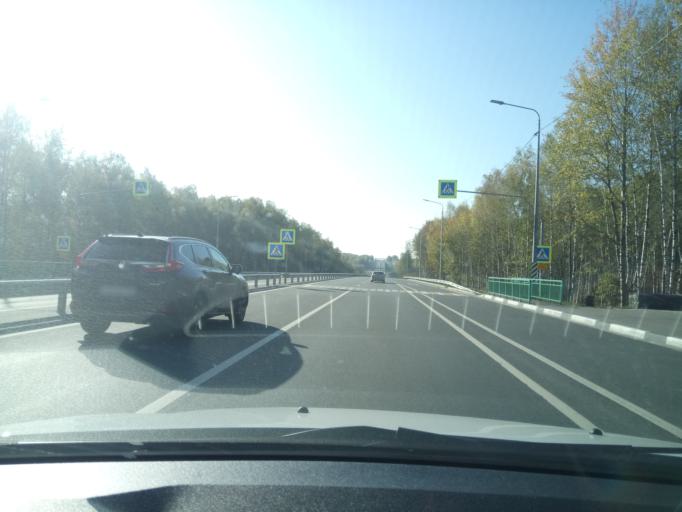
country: RU
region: Nizjnij Novgorod
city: Burevestnik
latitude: 56.0159
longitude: 43.9649
